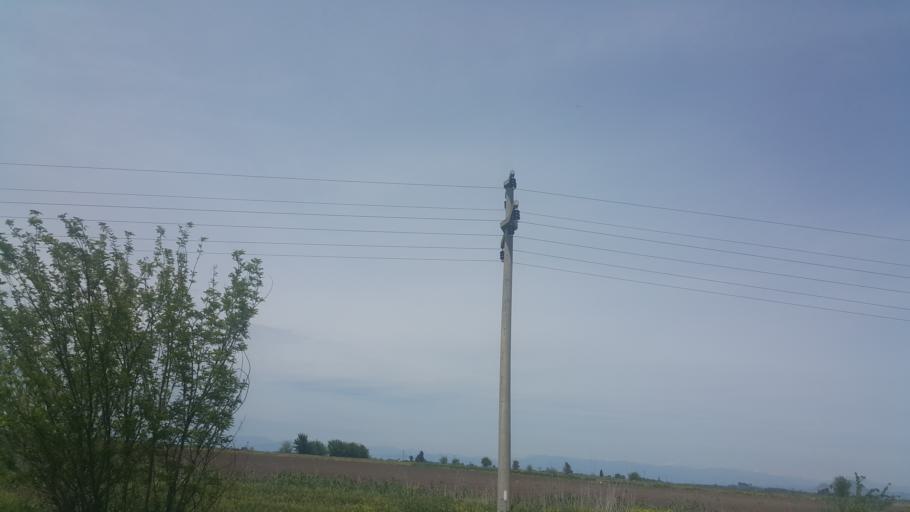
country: TR
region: Adana
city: Kosreli
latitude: 37.0723
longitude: 36.0344
